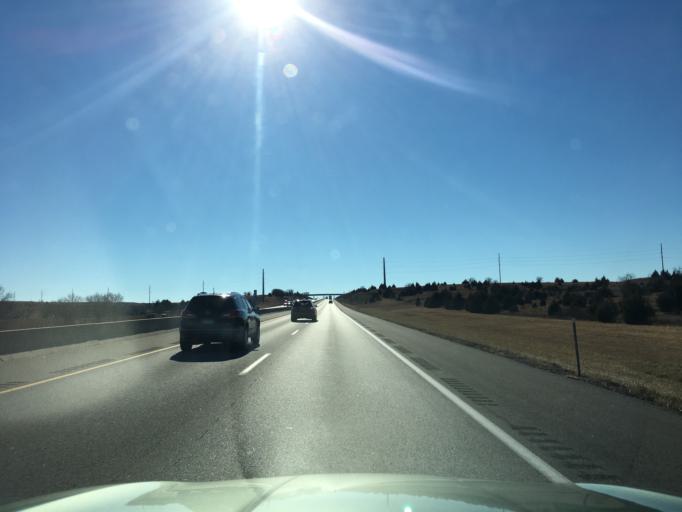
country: US
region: Kansas
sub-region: Sumner County
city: Wellington
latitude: 37.2106
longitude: -97.3400
